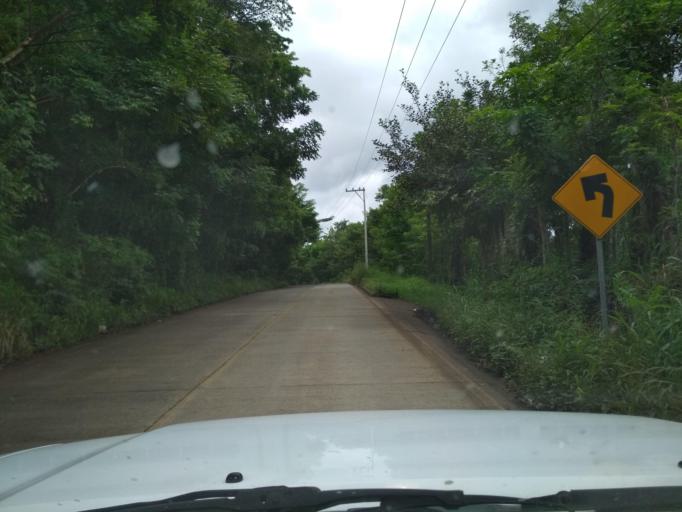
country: MX
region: Veracruz
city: Comoapan
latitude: 18.4162
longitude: -95.1776
